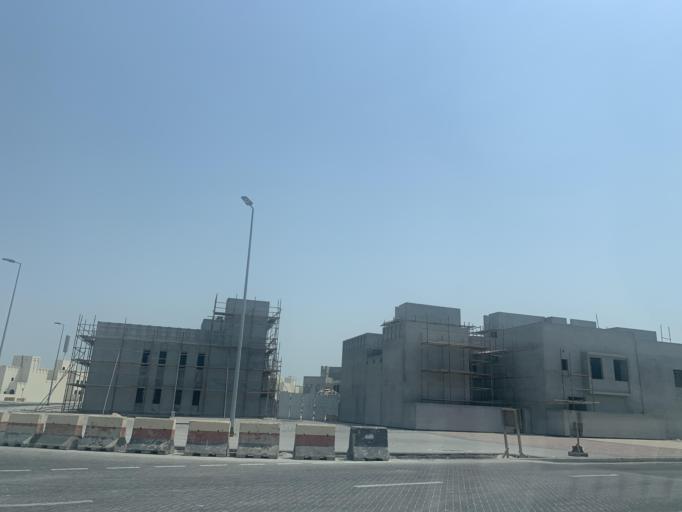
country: BH
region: Muharraq
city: Al Hadd
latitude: 26.2399
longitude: 50.6656
